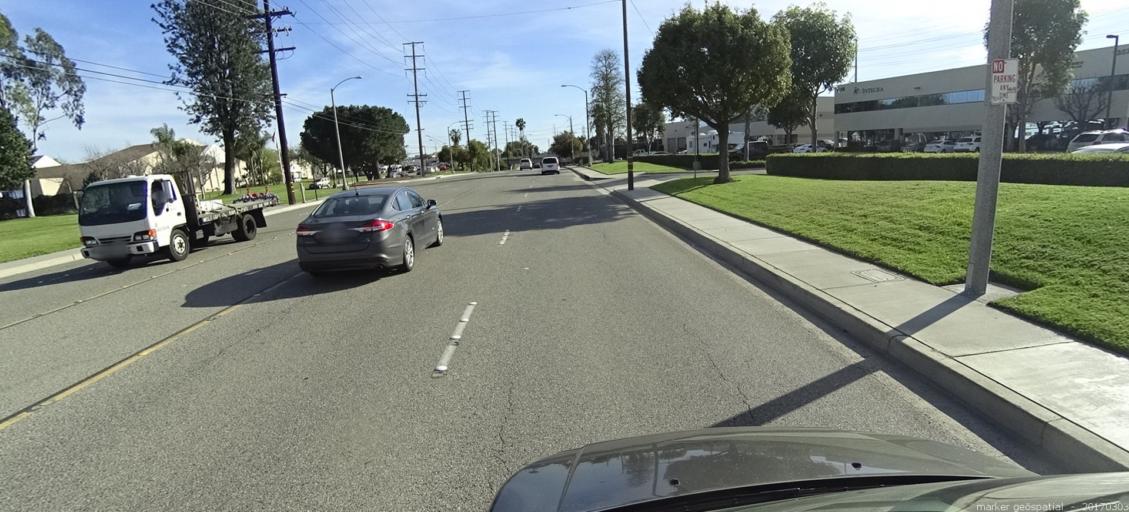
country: US
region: California
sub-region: Orange County
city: Anaheim
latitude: 33.8154
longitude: -117.8981
